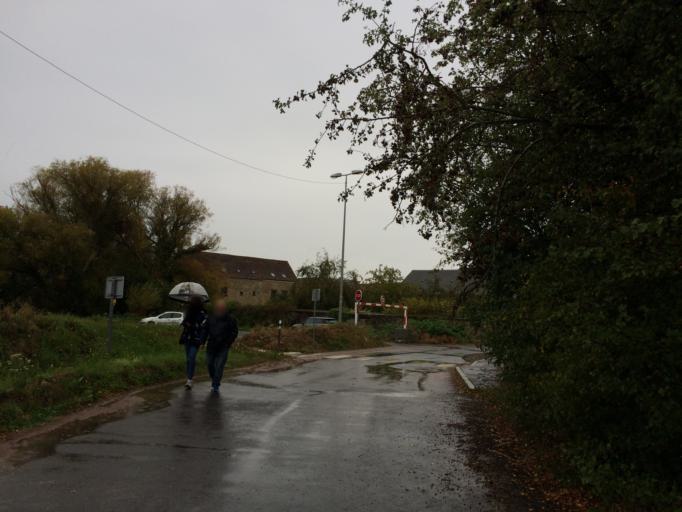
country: FR
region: Ile-de-France
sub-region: Departement de l'Essonne
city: Bures-sur-Yvette
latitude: 48.7087
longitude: 2.1598
